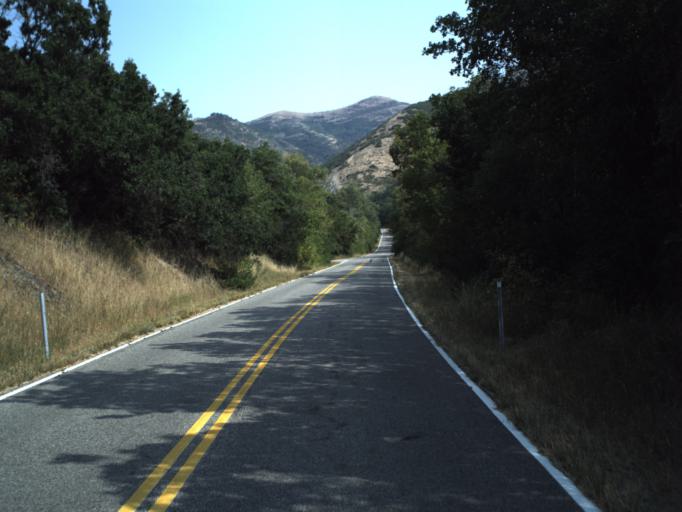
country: US
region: Utah
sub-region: Summit County
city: Summit Park
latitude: 40.7979
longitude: -111.6802
